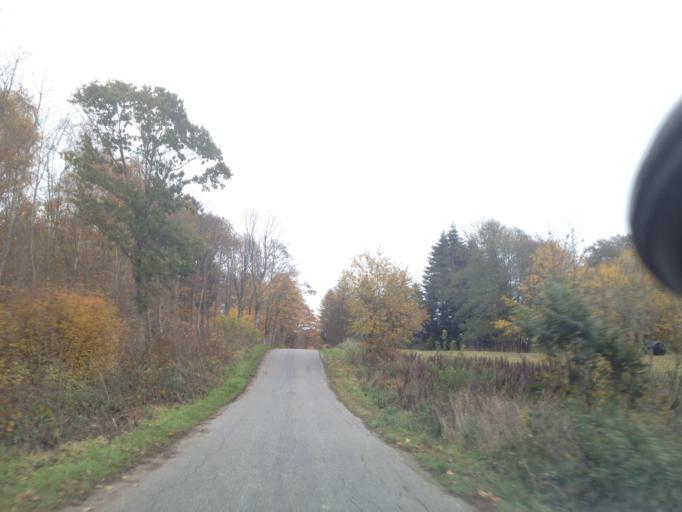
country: DK
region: South Denmark
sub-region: Nordfyns Kommune
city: Sonderso
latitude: 55.4257
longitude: 10.2063
